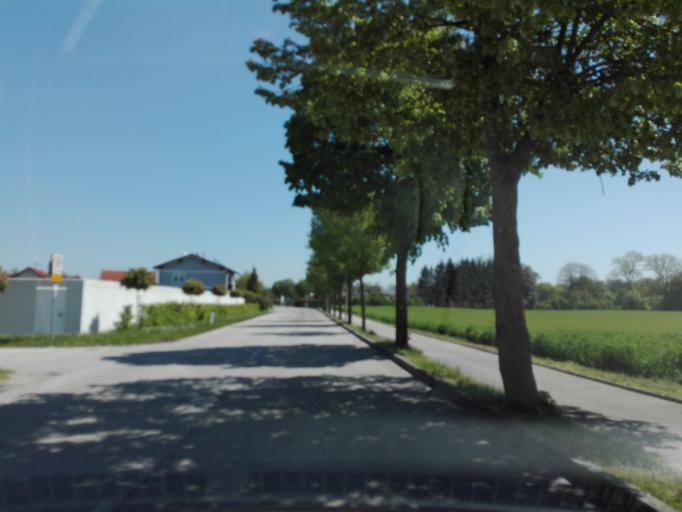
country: AT
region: Upper Austria
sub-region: Politischer Bezirk Linz-Land
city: Traun
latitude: 48.2097
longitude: 14.2081
